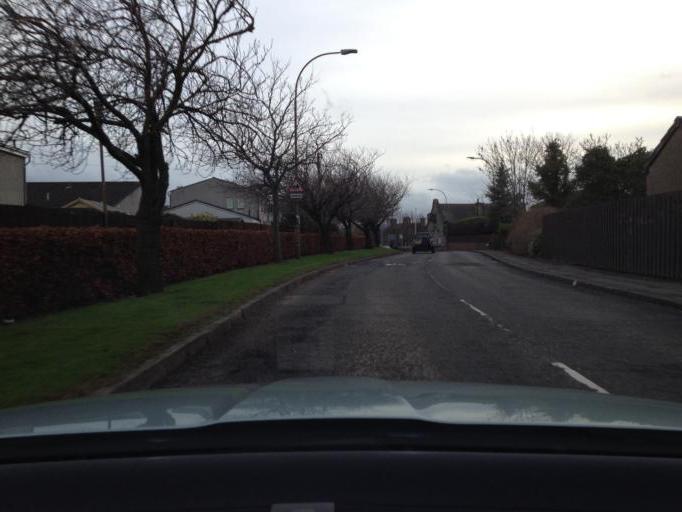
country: GB
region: Scotland
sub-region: Edinburgh
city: Kirkliston
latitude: 55.9589
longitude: -3.4033
